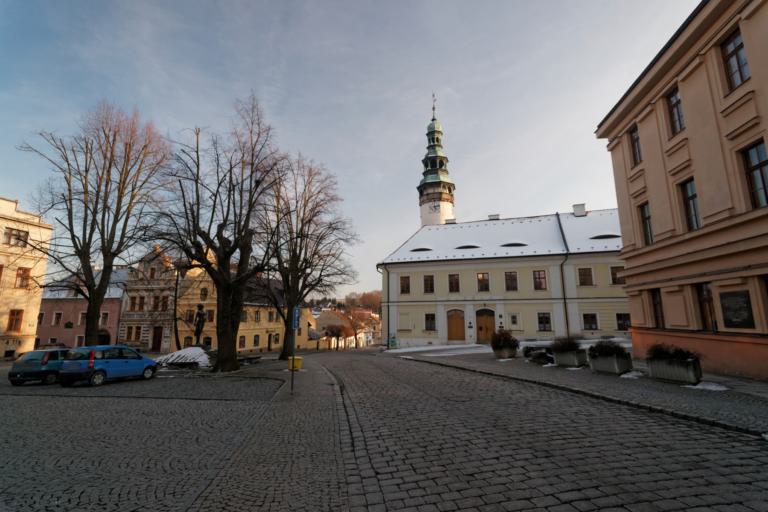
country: CZ
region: Plzensky
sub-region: Okres Domazlice
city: Domazlice
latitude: 49.4396
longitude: 12.9277
